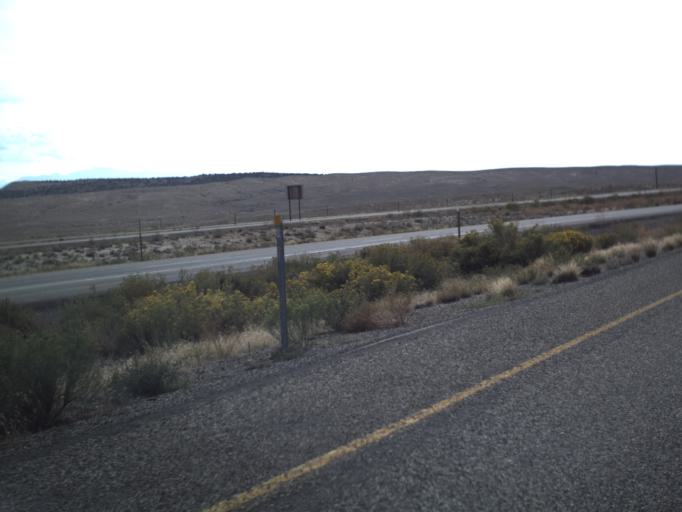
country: US
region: Colorado
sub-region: Mesa County
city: Loma
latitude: 39.1126
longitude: -109.1864
